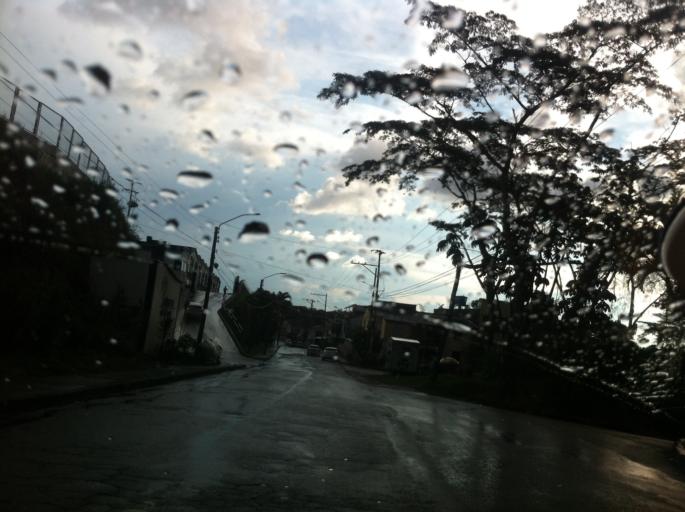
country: CO
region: Quindio
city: Armenia
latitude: 4.5573
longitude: -75.6661
